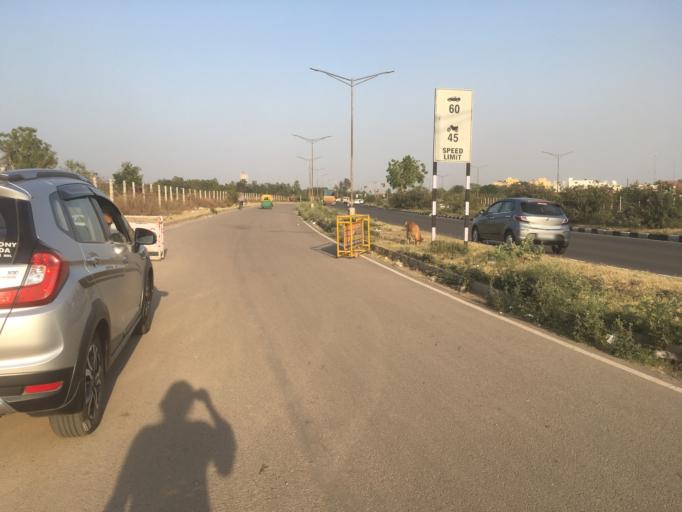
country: IN
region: Chandigarh
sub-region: Chandigarh
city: Chandigarh
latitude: 30.6894
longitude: 76.8218
